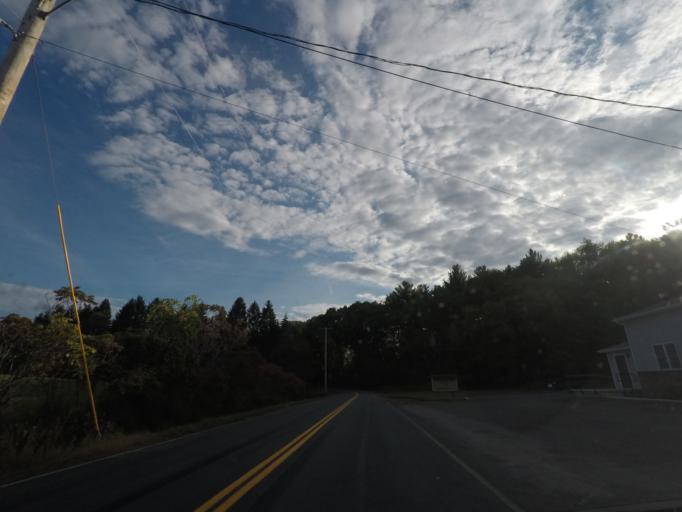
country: US
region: New York
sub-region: Rensselaer County
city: West Sand Lake
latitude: 42.6190
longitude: -73.6378
